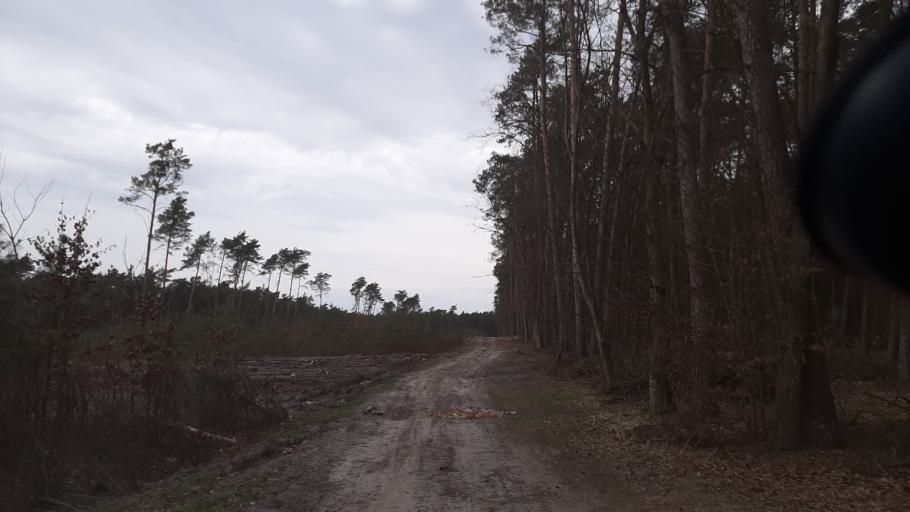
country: PL
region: Lublin Voivodeship
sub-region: Powiat lubelski
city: Garbow
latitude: 51.3949
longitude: 22.3785
